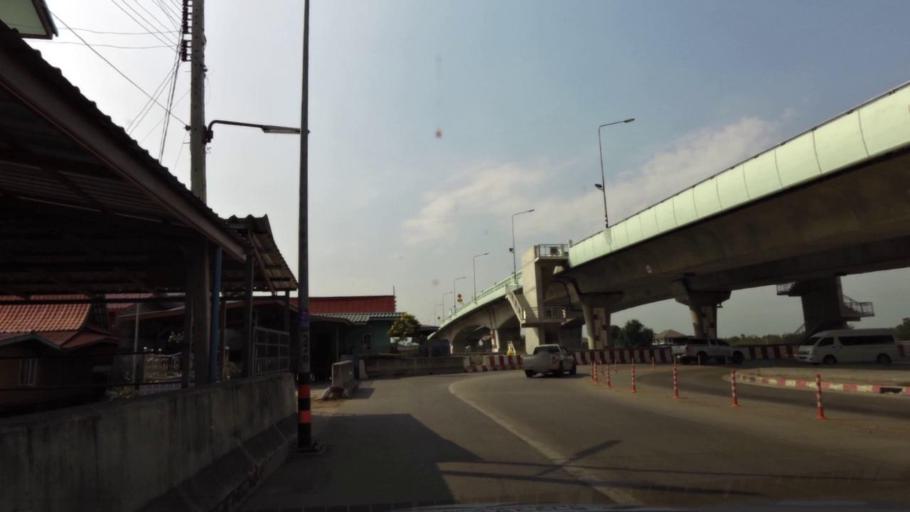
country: TH
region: Phra Nakhon Si Ayutthaya
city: Phra Nakhon Si Ayutthaya
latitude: 14.3325
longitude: 100.5784
